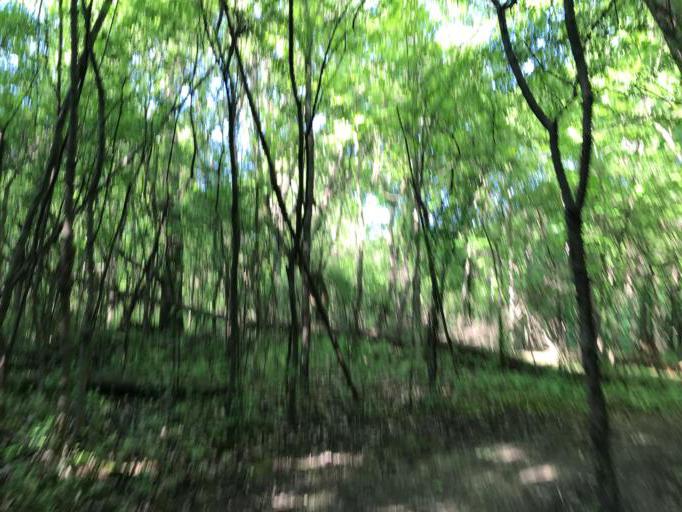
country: US
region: Michigan
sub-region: Oakland County
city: Farmington Hills
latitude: 42.4930
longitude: -83.3862
